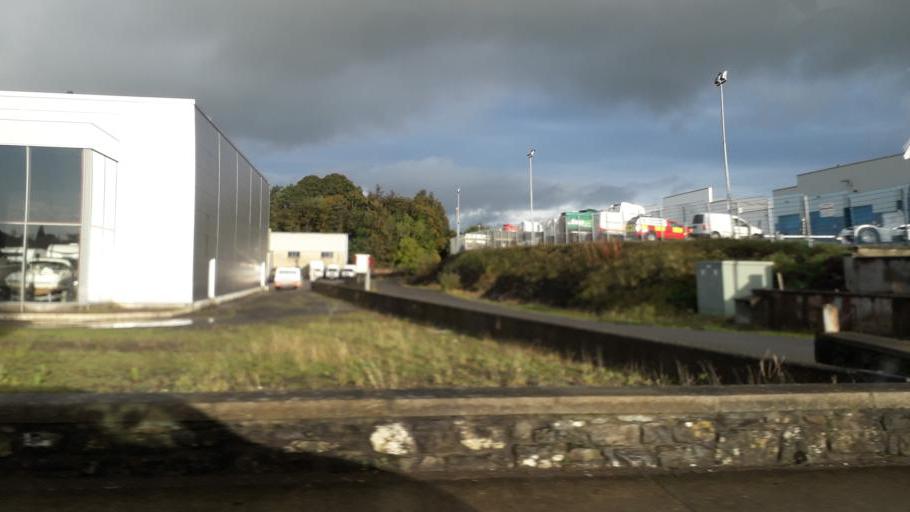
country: IE
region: Leinster
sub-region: An Longfort
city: Lanesborough
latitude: 53.7745
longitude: -8.1033
